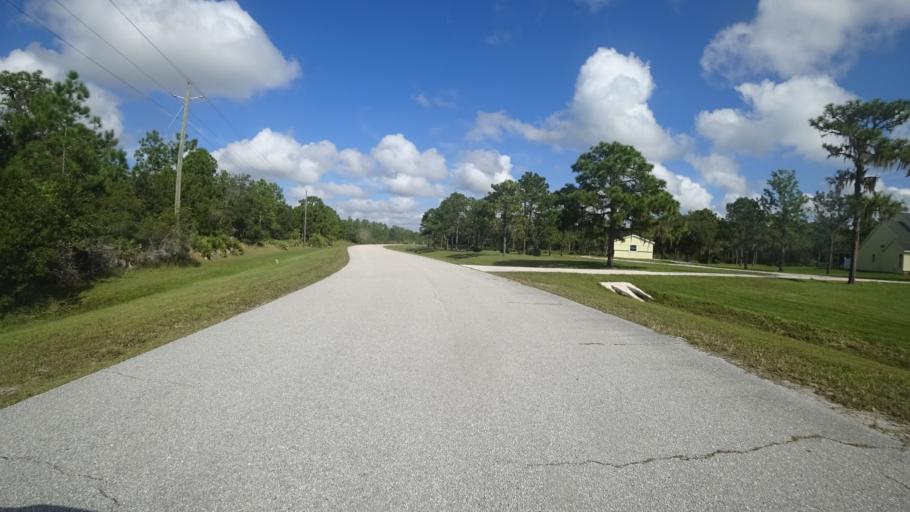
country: US
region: Florida
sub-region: Sarasota County
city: The Meadows
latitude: 27.3988
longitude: -82.3396
